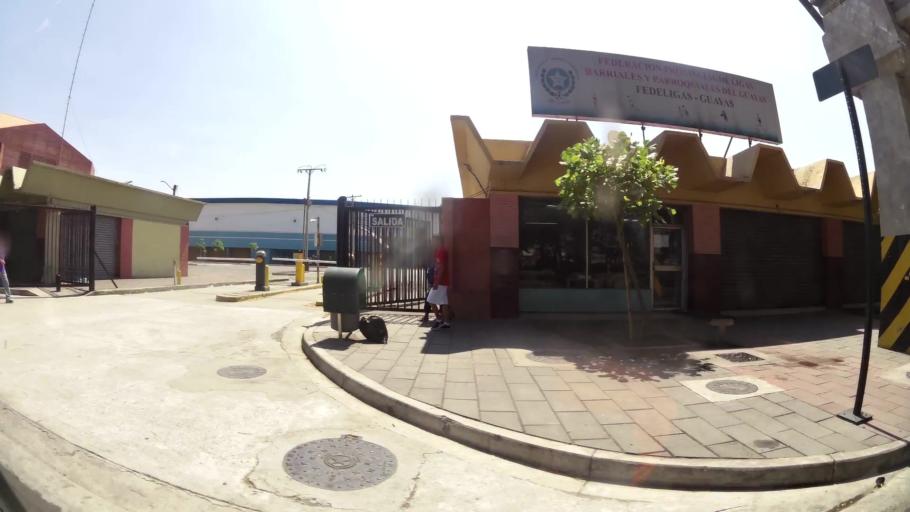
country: EC
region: Guayas
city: Guayaquil
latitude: -2.1807
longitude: -79.8944
